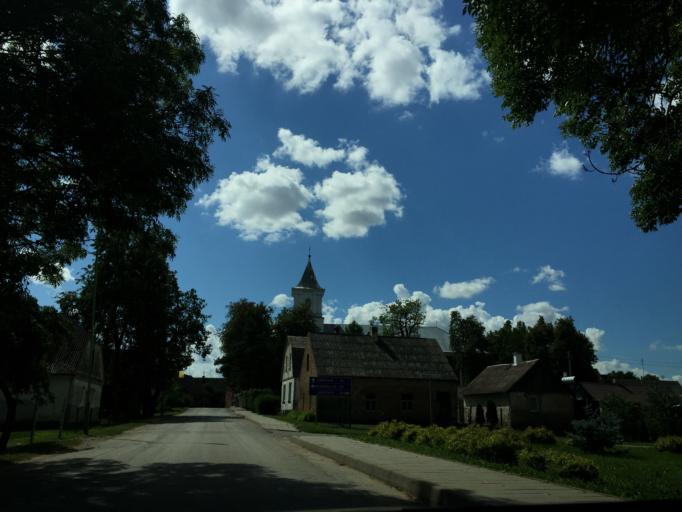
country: LV
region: Rundales
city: Pilsrundale
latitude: 56.2743
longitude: 24.0001
